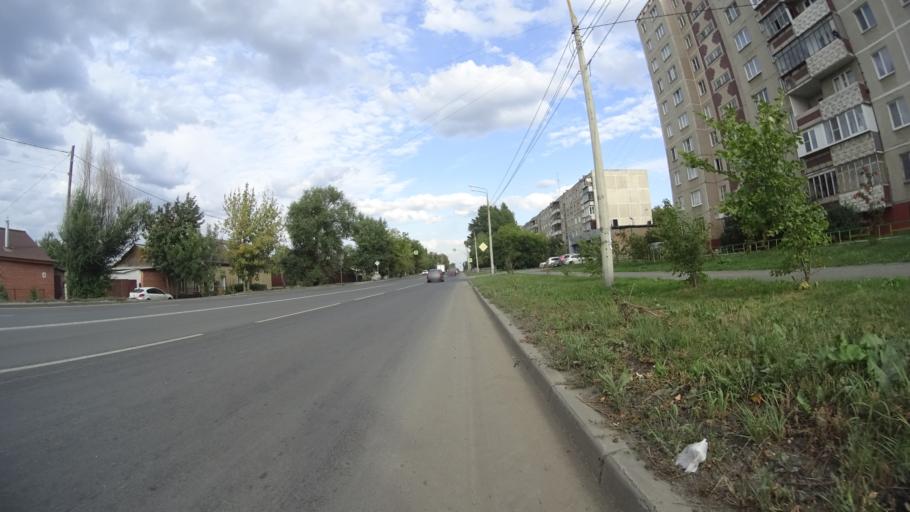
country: RU
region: Chelyabinsk
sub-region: Gorod Chelyabinsk
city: Chelyabinsk
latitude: 55.1985
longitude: 61.3484
